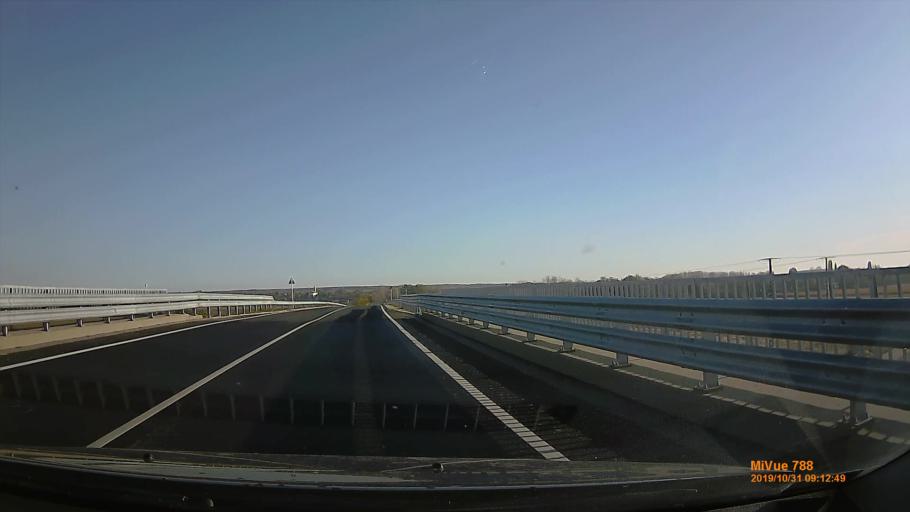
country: HU
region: Pest
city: Peteri
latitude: 47.3775
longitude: 19.3988
